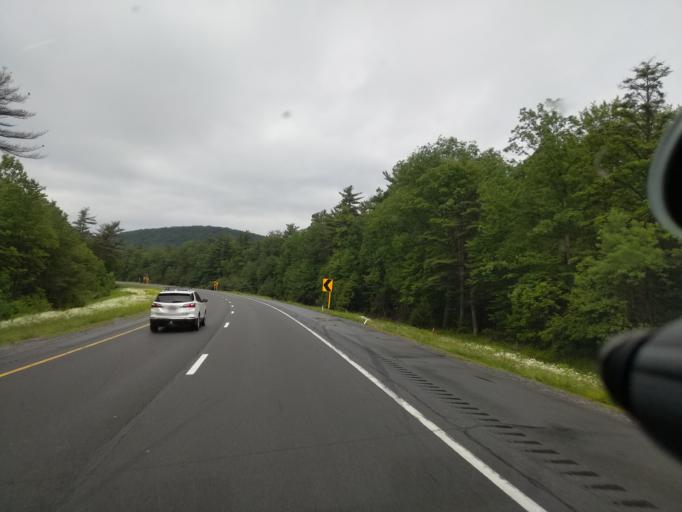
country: US
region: Pennsylvania
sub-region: Union County
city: Mifflinburg
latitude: 41.0493
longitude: -77.1462
